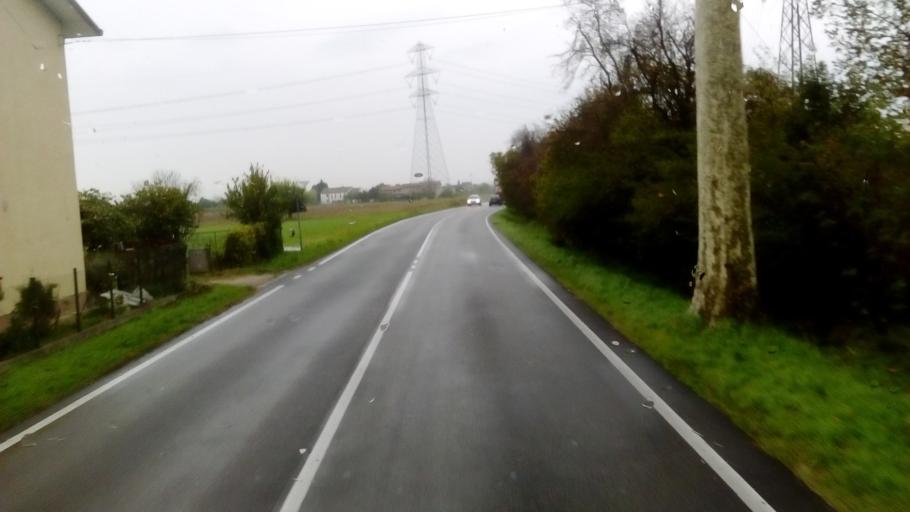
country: IT
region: Veneto
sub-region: Provincia di Vicenza
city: Montecchio Precalcino
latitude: 45.6760
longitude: 11.5717
